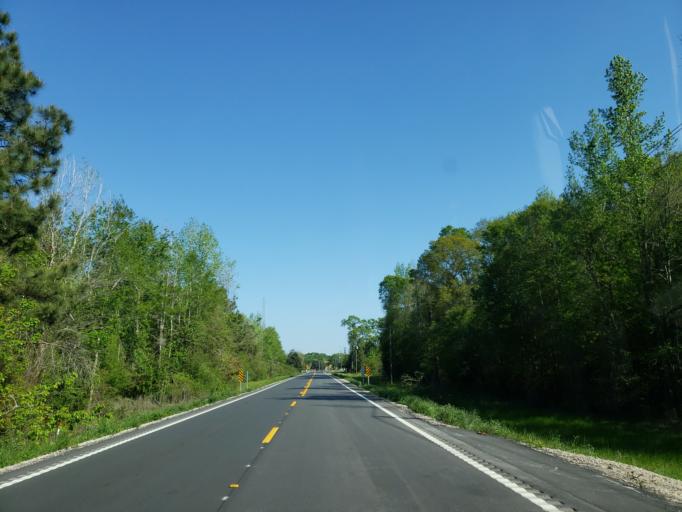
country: US
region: Mississippi
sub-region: Perry County
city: New Augusta
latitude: 31.1725
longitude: -88.9250
